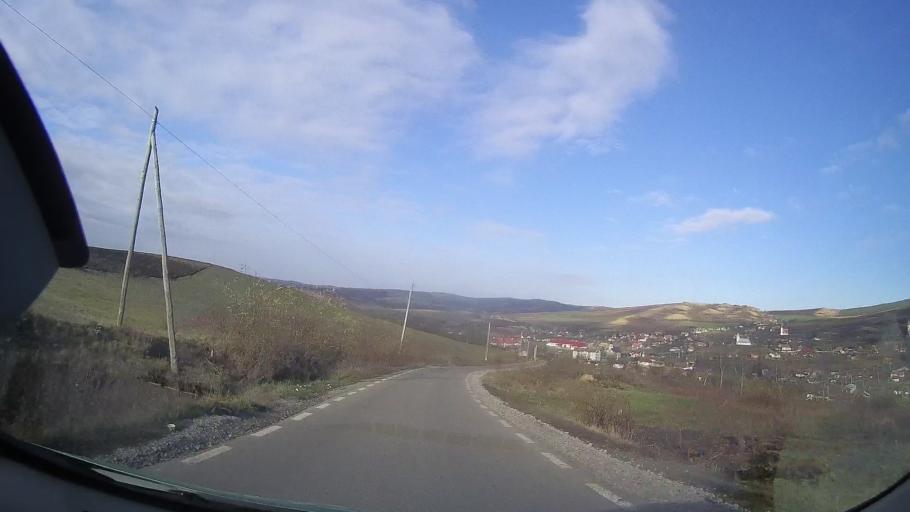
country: RO
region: Mures
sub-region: Comuna Sanger
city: Sanger
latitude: 46.5527
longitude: 24.1431
